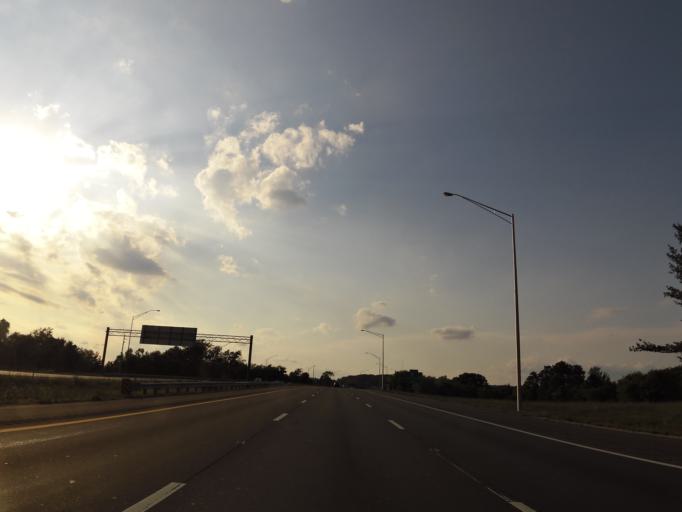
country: US
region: Tennessee
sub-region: Knox County
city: Knoxville
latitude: 35.9664
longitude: -83.9775
